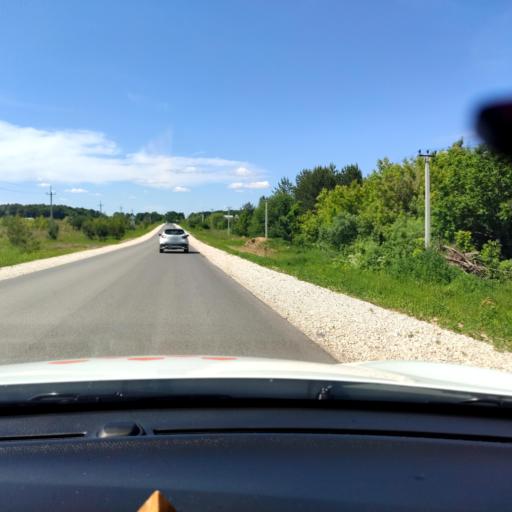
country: RU
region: Tatarstan
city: Osinovo
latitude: 55.7731
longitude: 48.8226
